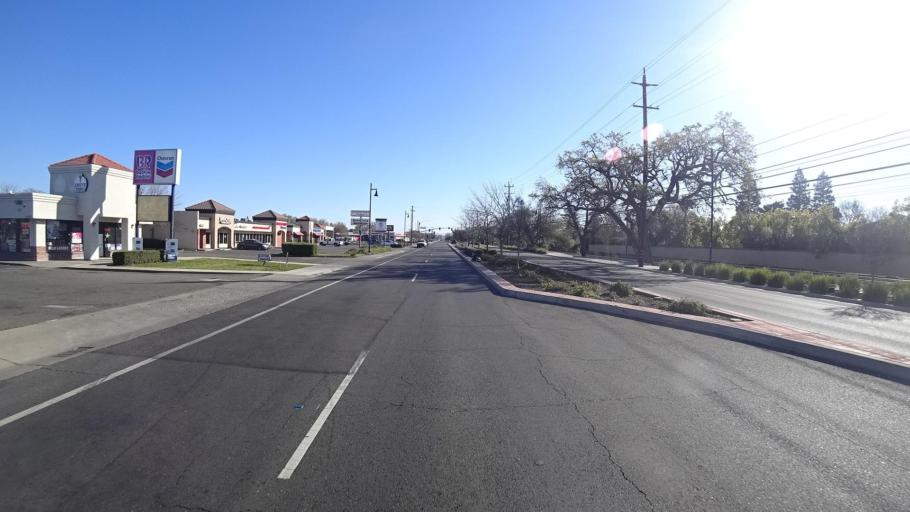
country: US
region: California
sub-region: Sacramento County
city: Rancho Cordova
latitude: 38.5821
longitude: -121.3176
